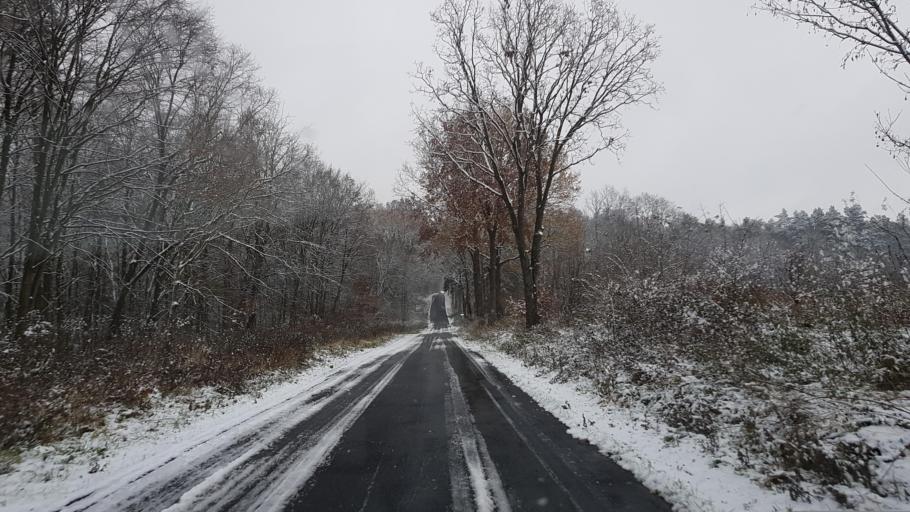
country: PL
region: West Pomeranian Voivodeship
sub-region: Powiat lobeski
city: Resko
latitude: 53.7703
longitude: 15.5322
